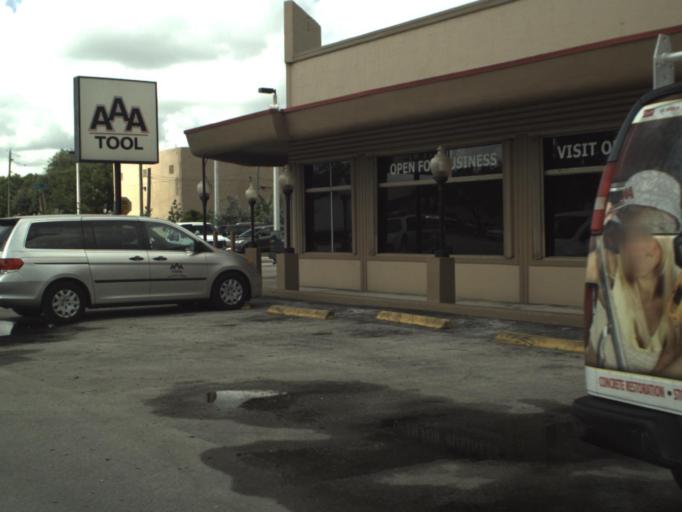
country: US
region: Florida
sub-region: Broward County
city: West Park
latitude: 25.9978
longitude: -80.2072
